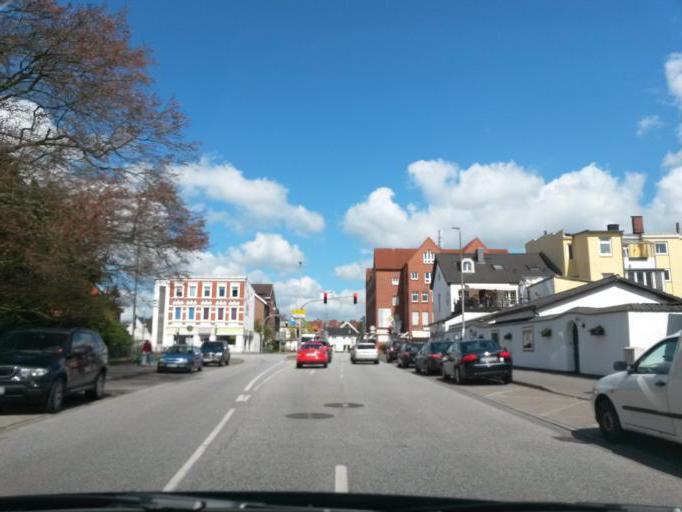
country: DE
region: Schleswig-Holstein
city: Uetersen
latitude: 53.6834
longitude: 9.6631
